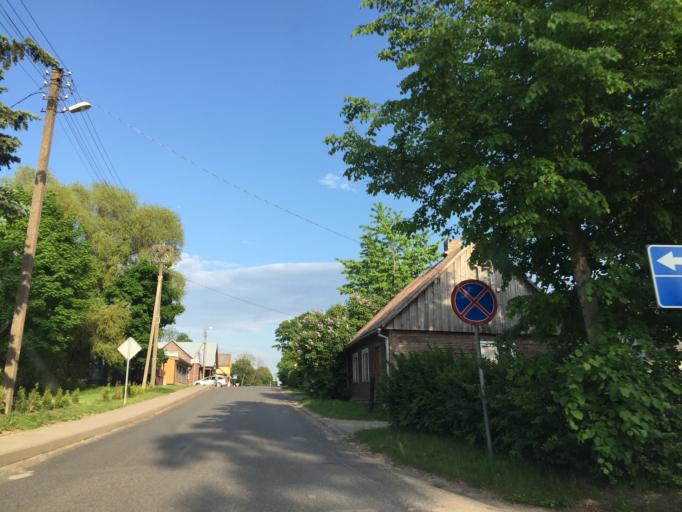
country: LT
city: Plateliai
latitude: 56.0435
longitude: 21.8140
